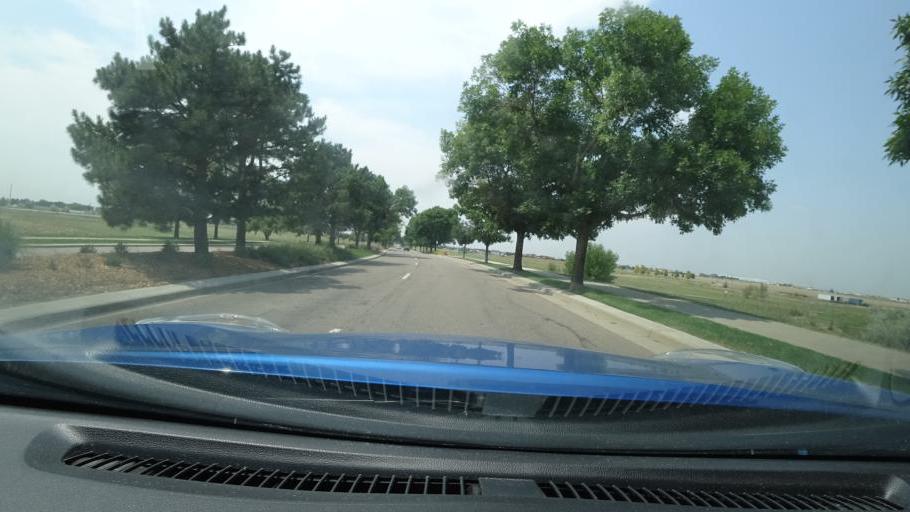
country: US
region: Colorado
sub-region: Adams County
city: Aurora
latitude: 39.7617
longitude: -104.7650
